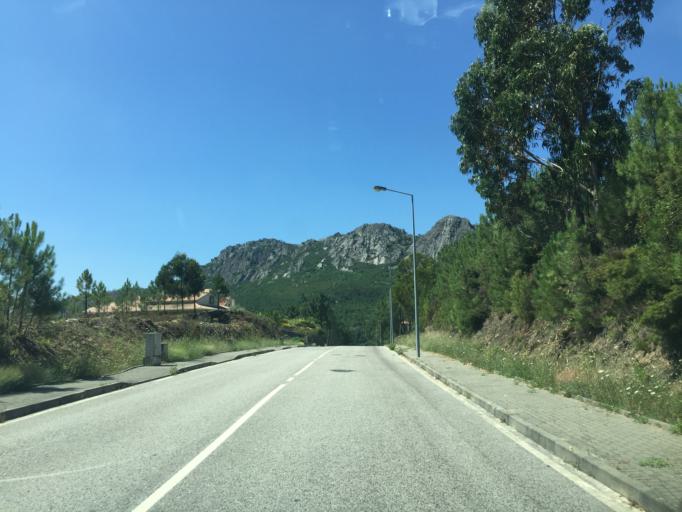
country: PT
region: Coimbra
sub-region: Pampilhosa da Serra
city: Pampilhosa da Serra
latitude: 40.0938
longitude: -7.8486
